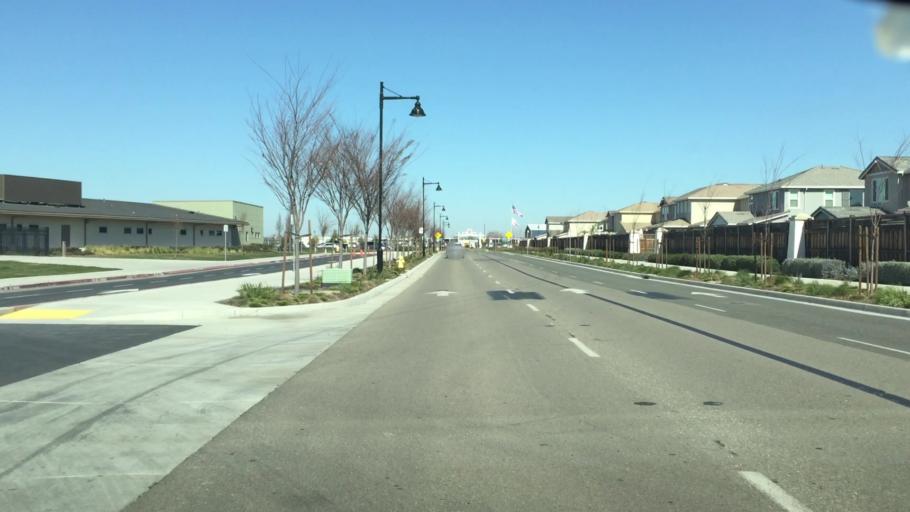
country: US
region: California
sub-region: San Joaquin County
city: Lathrop
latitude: 37.7964
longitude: -121.3185
